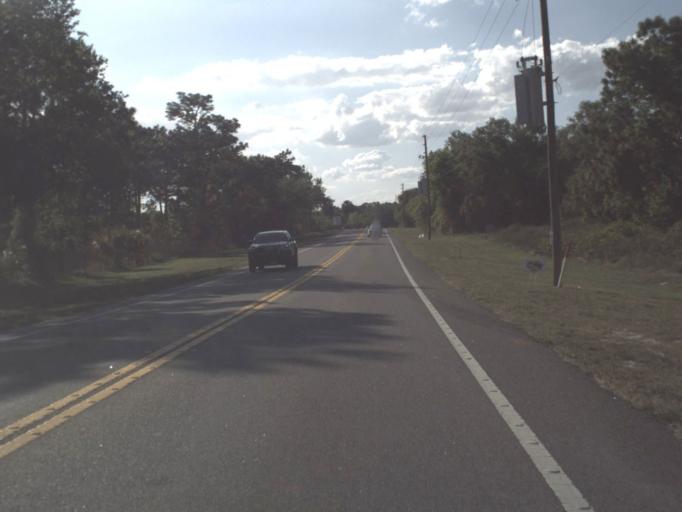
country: US
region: Florida
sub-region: Lake County
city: Mount Plymouth
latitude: 28.8149
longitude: -81.4701
